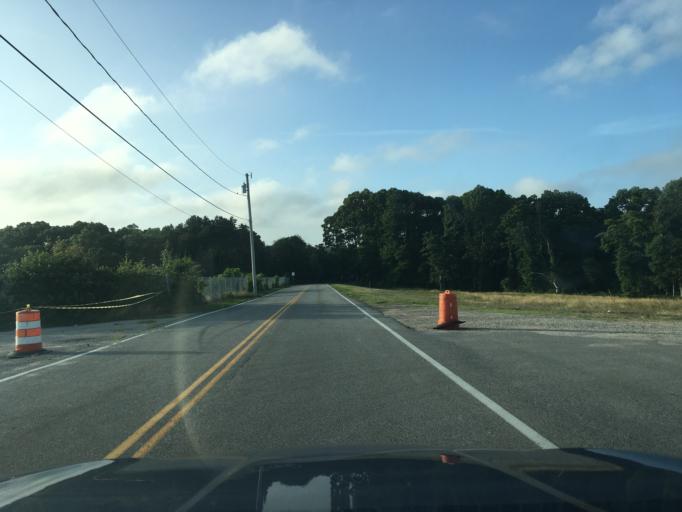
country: US
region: Rhode Island
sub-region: Kent County
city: East Greenwich
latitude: 41.6181
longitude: -71.4230
